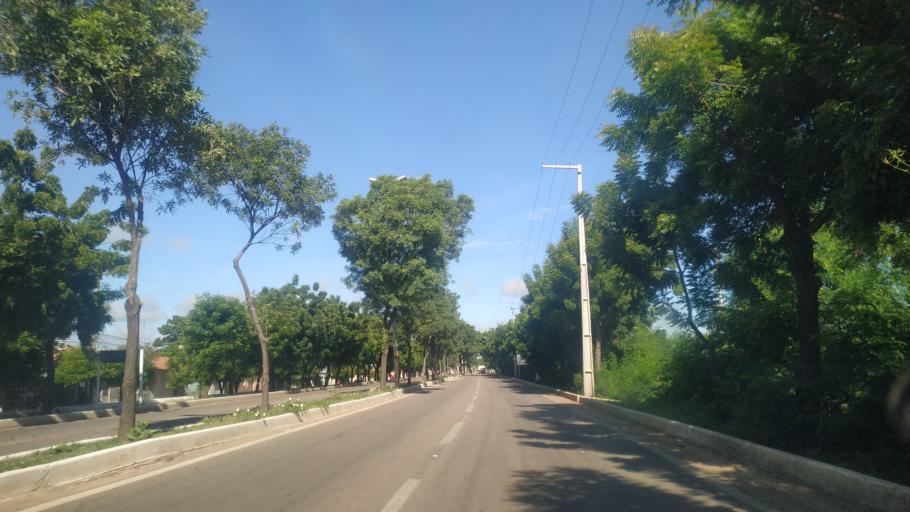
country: BR
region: Rio Grande do Norte
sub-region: Mossoro
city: Mossoro
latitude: -5.1918
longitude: -37.3639
